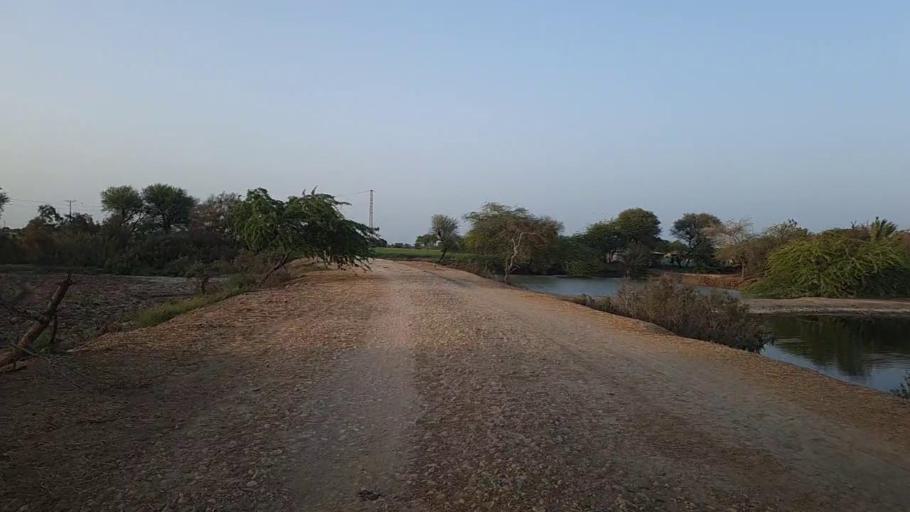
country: PK
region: Sindh
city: Kario
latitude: 24.7206
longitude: 68.4630
